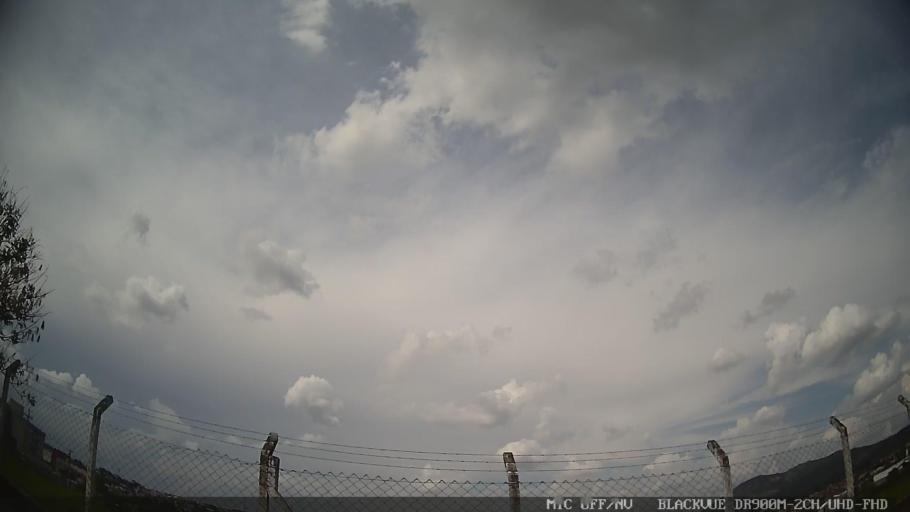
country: BR
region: Sao Paulo
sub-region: Braganca Paulista
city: Braganca Paulista
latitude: -22.9394
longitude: -46.5269
